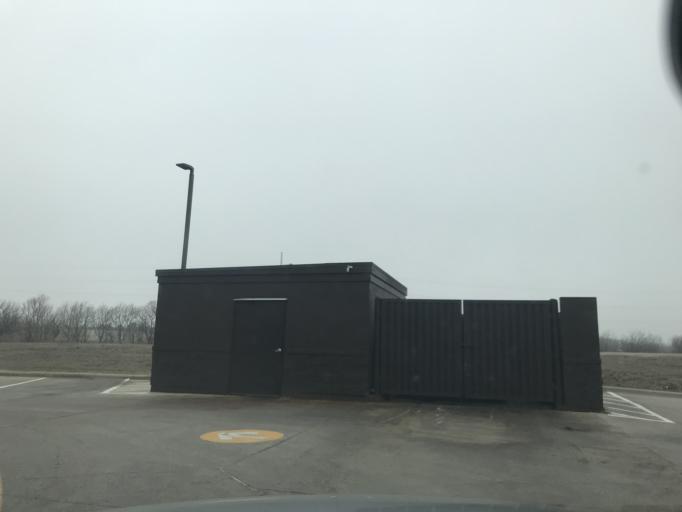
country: US
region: Texas
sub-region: Rockwall County
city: Royse City
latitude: 32.9699
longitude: -96.3328
